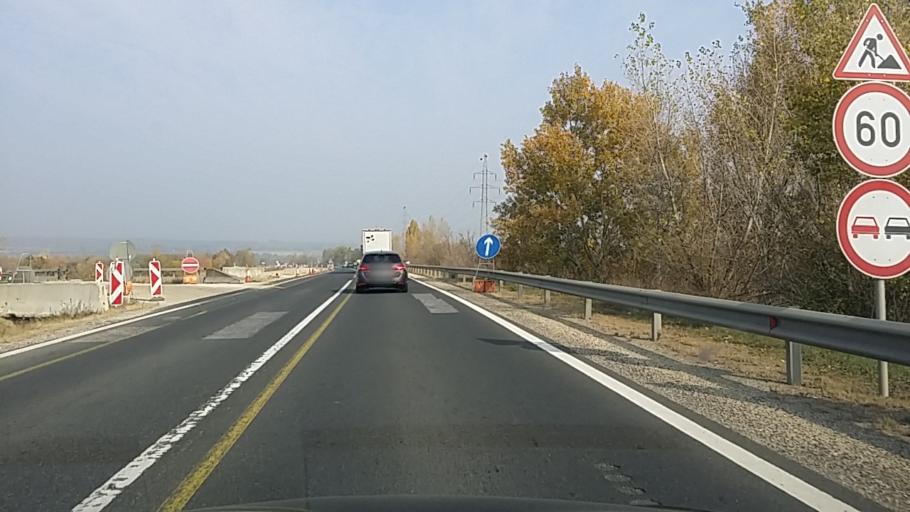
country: HU
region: Pest
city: Szod
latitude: 47.7469
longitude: 19.1767
